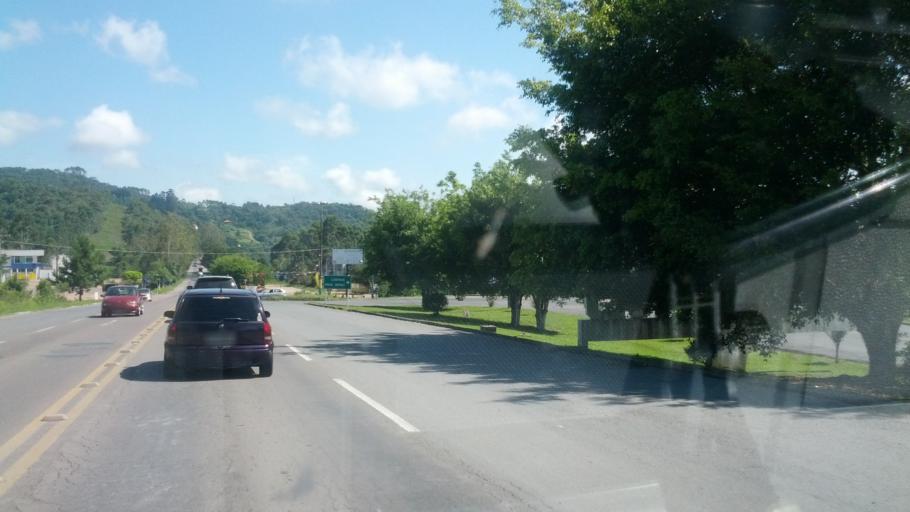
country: BR
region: Santa Catarina
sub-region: Rio Do Sul
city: Rio do Sul
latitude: -27.1613
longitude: -49.5566
